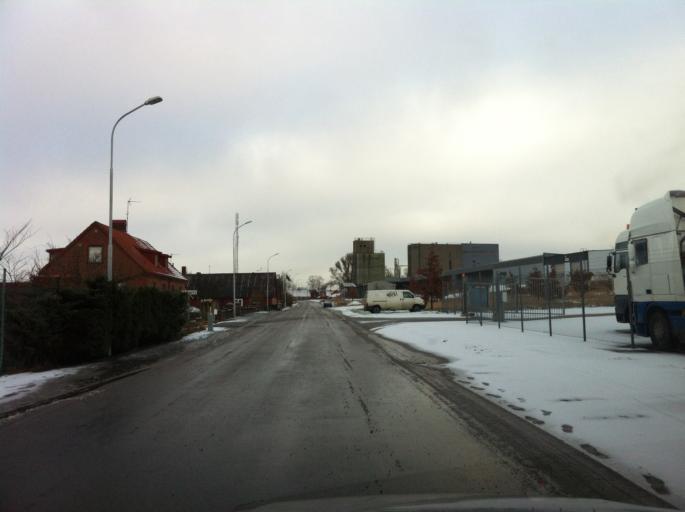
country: SE
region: Skane
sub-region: Svalovs Kommun
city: Svaloev
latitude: 55.9066
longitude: 13.1078
